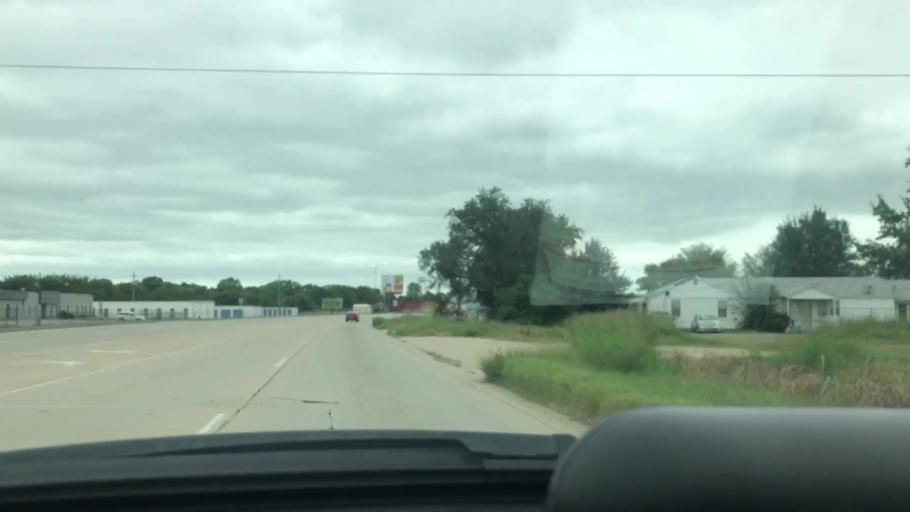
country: US
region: Oklahoma
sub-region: Mayes County
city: Chouteau
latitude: 36.1785
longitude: -95.3428
